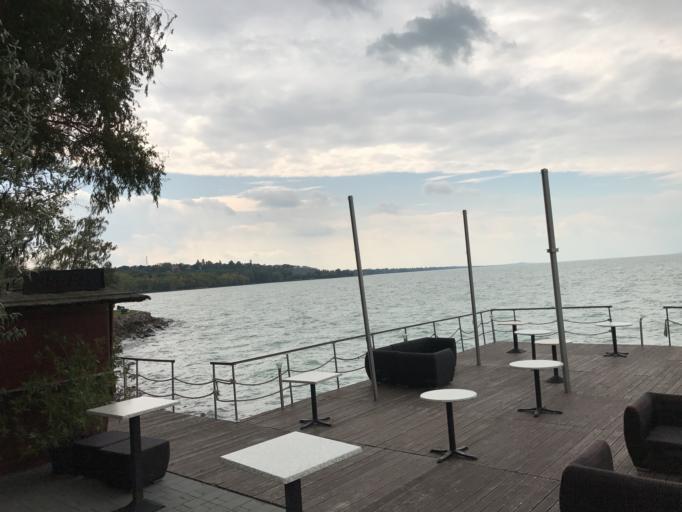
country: HU
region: Somogy
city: Balatonfoldvar
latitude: 46.8576
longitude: 17.8786
